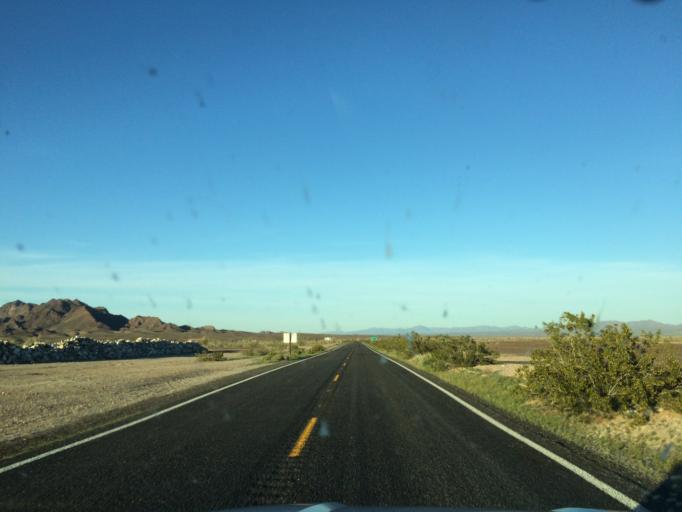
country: US
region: California
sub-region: Riverside County
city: Mesa Verde
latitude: 33.2700
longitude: -114.7962
